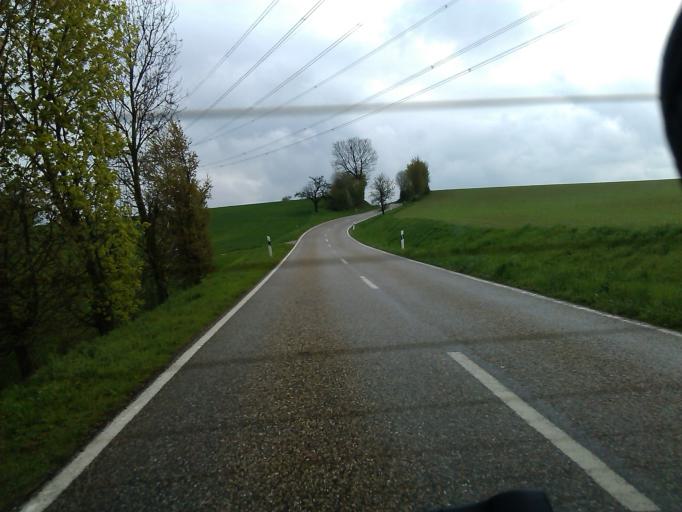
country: DE
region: Baden-Wuerttemberg
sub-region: Regierungsbezirk Stuttgart
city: Siegelsbach
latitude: 49.2645
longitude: 9.0998
